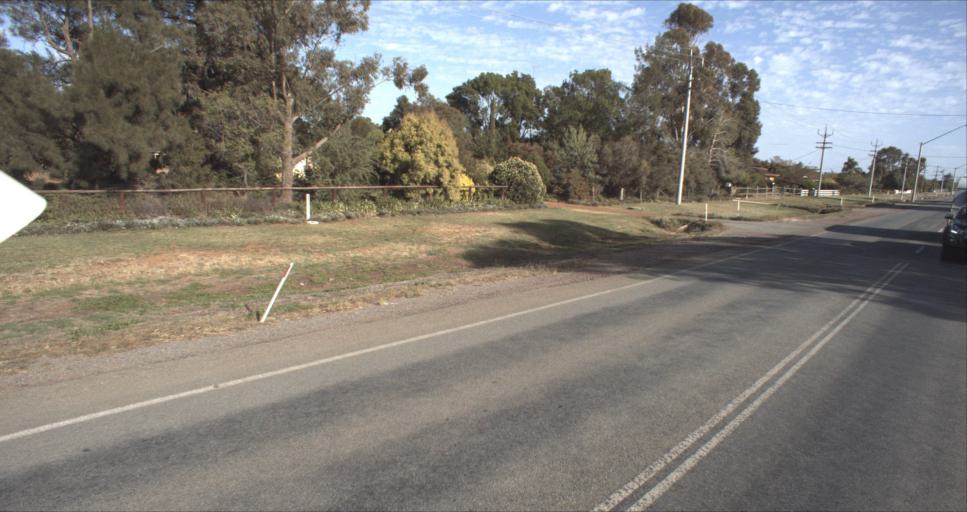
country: AU
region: New South Wales
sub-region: Leeton
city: Leeton
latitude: -34.5680
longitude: 146.3938
